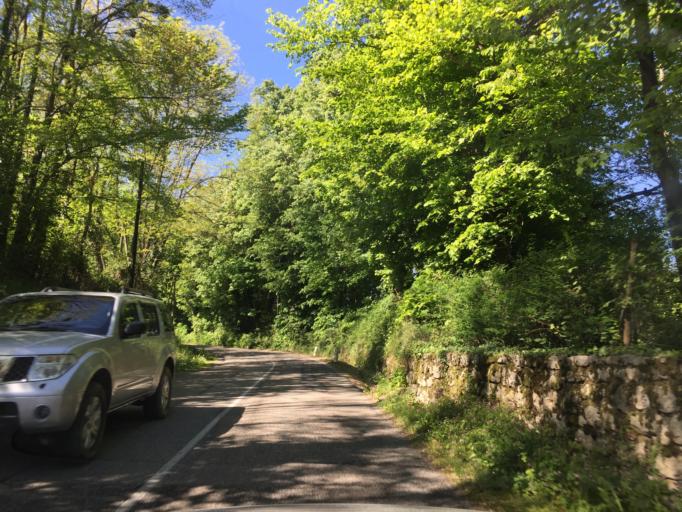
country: FR
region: Rhone-Alpes
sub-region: Departement de la Savoie
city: Cognin
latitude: 45.5649
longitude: 5.8883
